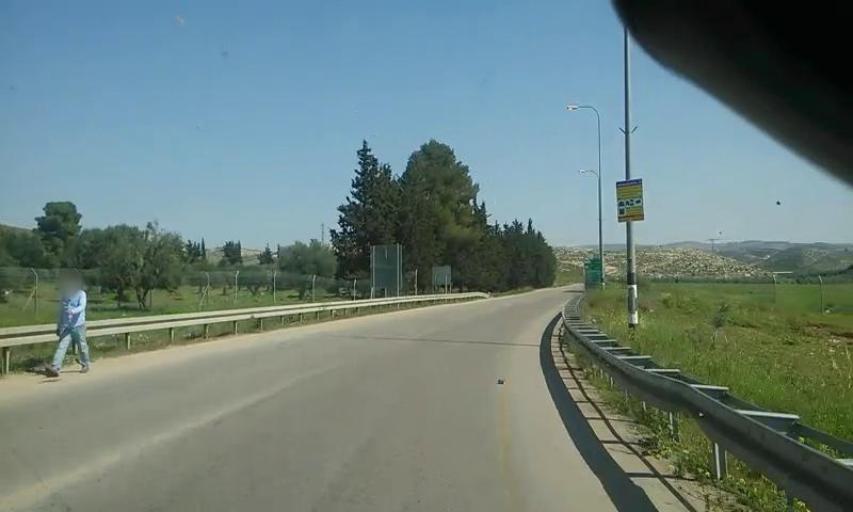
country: PS
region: West Bank
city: Idhna
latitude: 31.5905
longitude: 34.9655
